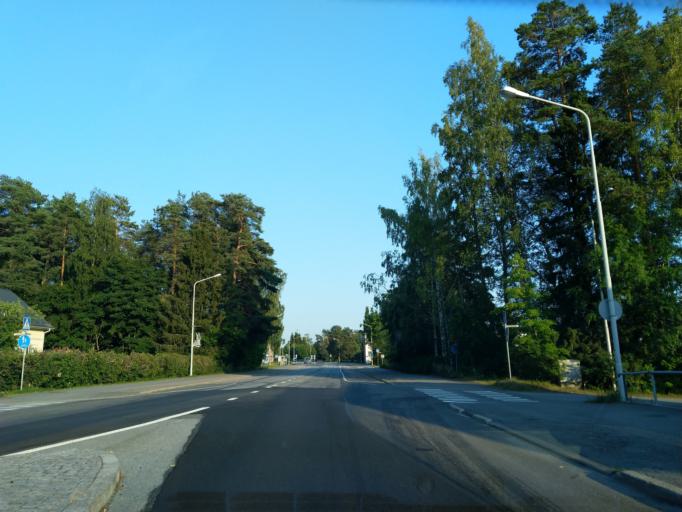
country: FI
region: Satakunta
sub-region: Pohjois-Satakunta
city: Kankaanpaeae
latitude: 61.8092
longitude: 22.3836
